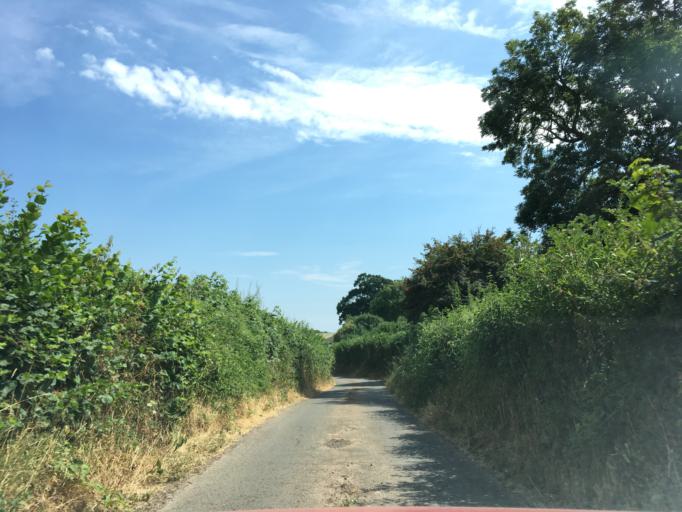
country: GB
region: Wales
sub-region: Monmouthshire
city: Magor
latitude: 51.5957
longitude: -2.8398
